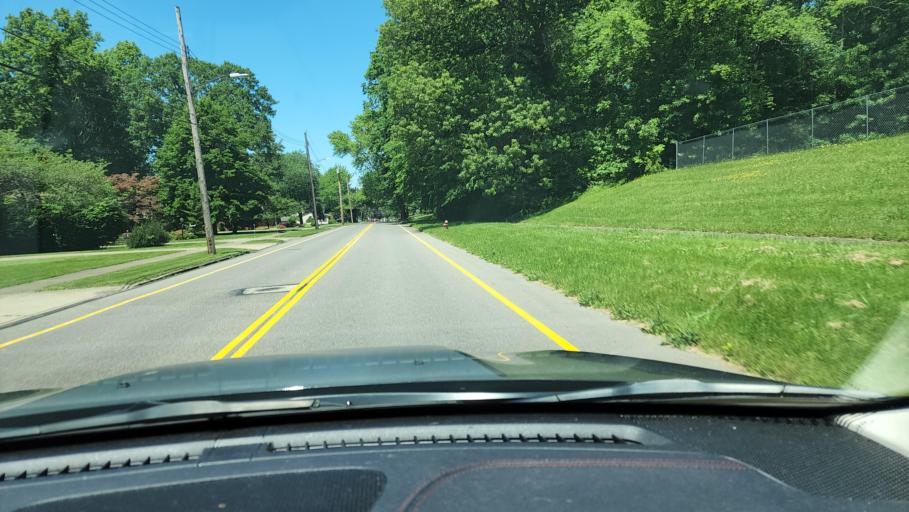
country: US
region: Ohio
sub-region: Trumbull County
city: Niles
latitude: 41.1908
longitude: -80.7447
